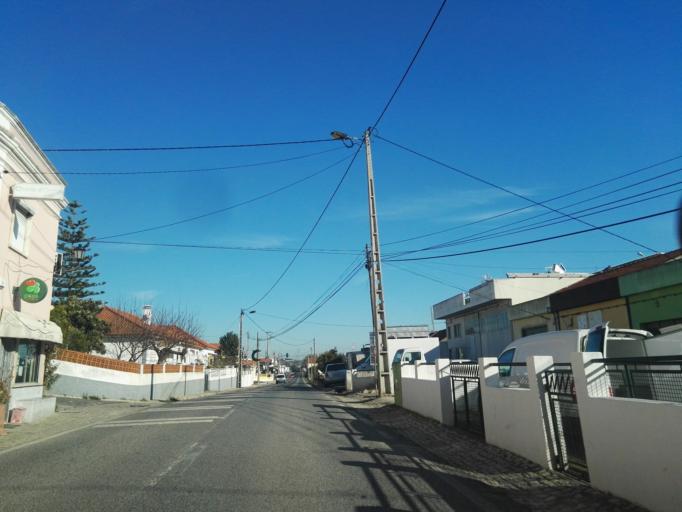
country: PT
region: Lisbon
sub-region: Vila Franca de Xira
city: Castanheira do Ribatejo
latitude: 39.0039
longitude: -9.0040
